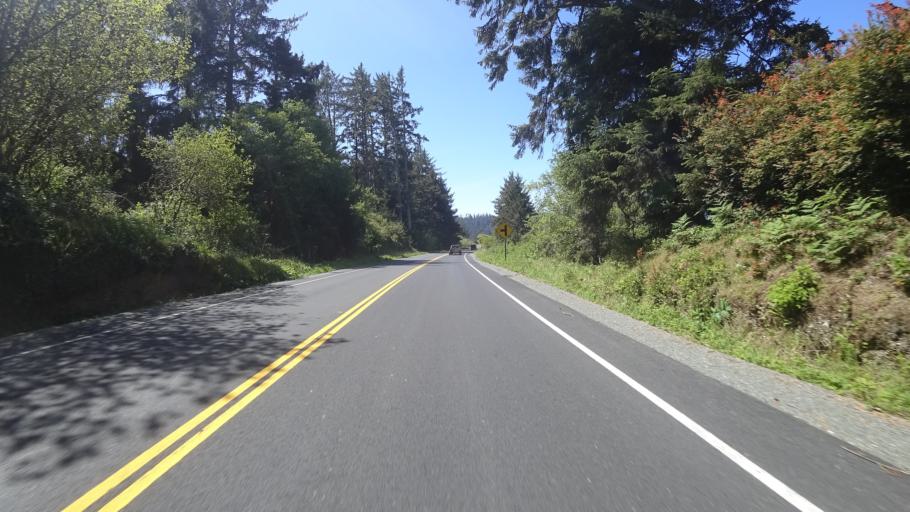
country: US
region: California
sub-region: Humboldt County
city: Westhaven-Moonstone
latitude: 41.1678
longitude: -124.1027
